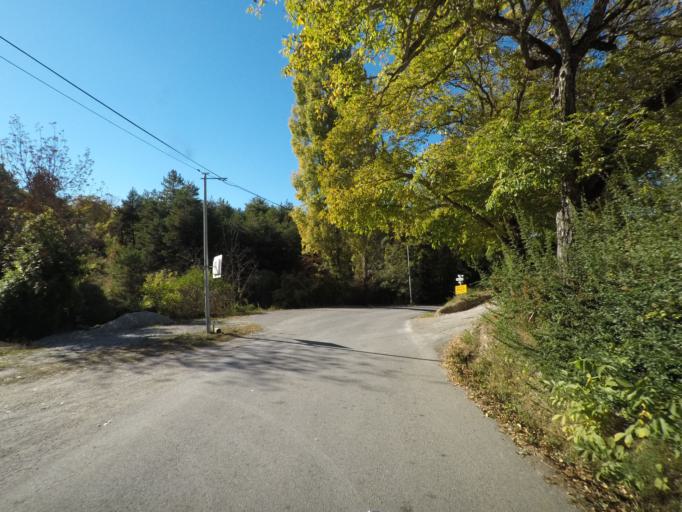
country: FR
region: Provence-Alpes-Cote d'Azur
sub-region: Departement des Hautes-Alpes
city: Serres
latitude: 44.4448
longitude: 5.5519
